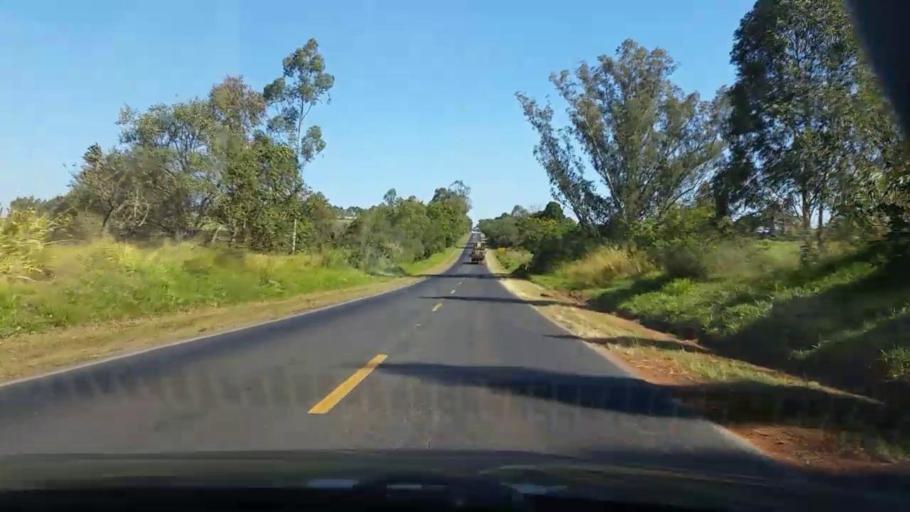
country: BR
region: Sao Paulo
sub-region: Sao Manuel
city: Sao Manuel
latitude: -22.8090
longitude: -48.6745
